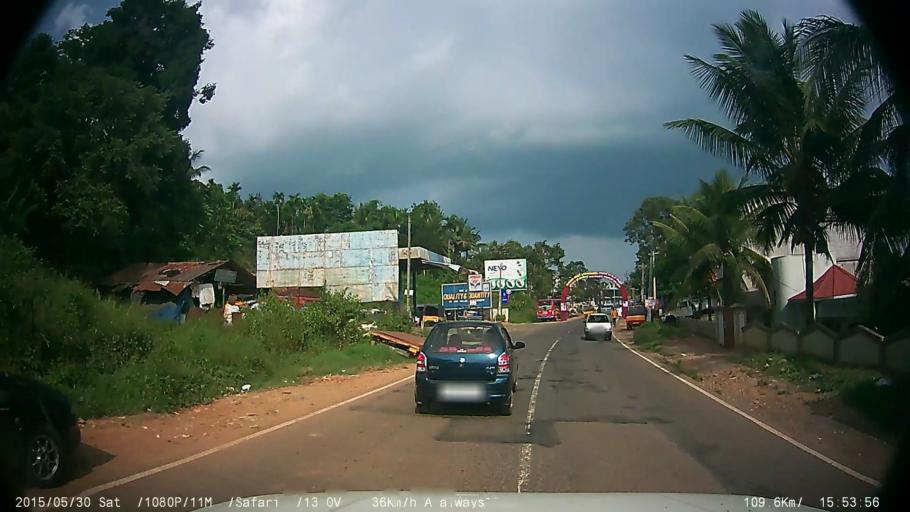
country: IN
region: Kerala
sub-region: Wayanad
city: Kalpetta
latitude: 11.6732
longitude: 76.0780
